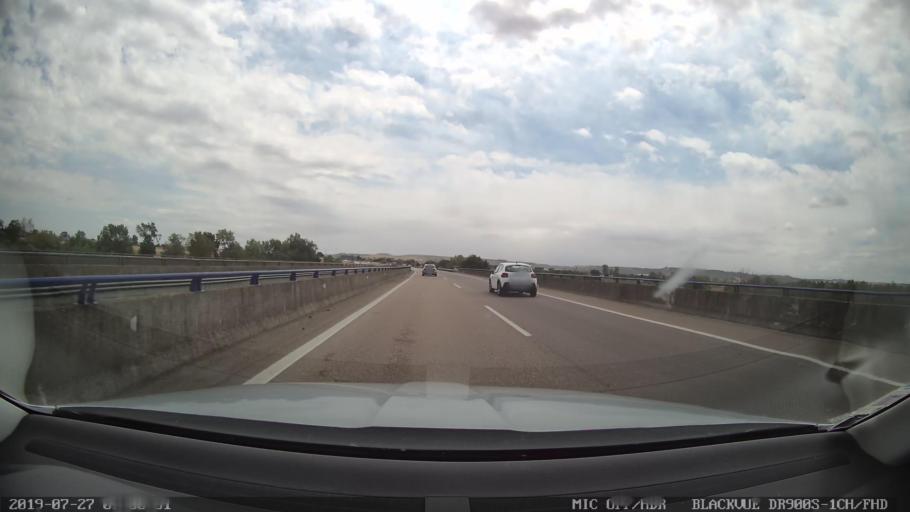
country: ES
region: Castille-La Mancha
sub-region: Province of Toledo
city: Talavera de la Reina
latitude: 39.9861
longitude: -4.7563
